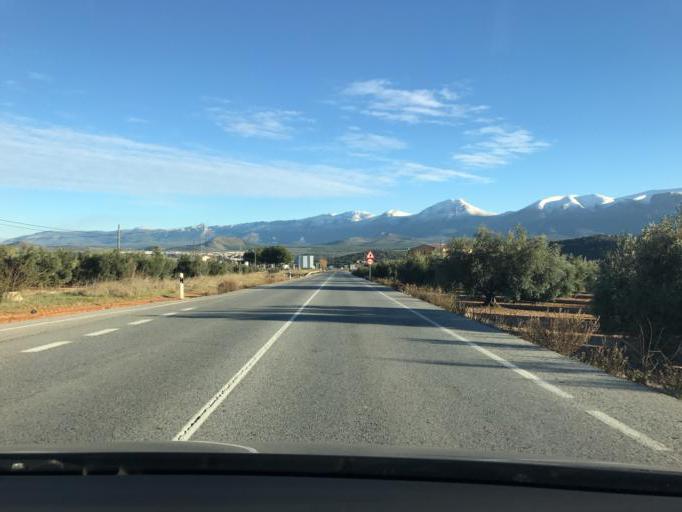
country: ES
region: Andalusia
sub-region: Provincia de Granada
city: Iznalloz
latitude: 37.4025
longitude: -3.5577
